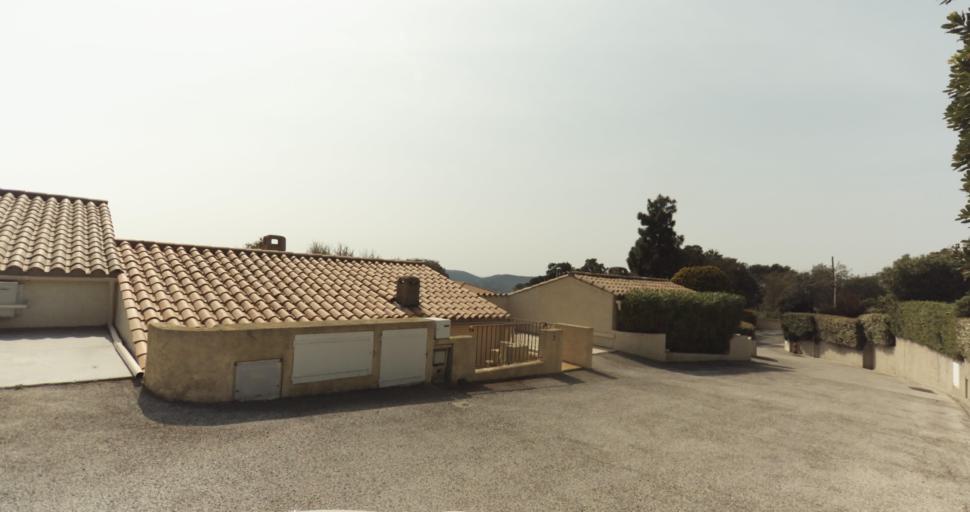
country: FR
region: Provence-Alpes-Cote d'Azur
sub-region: Departement du Var
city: Bormes-les-Mimosas
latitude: 43.1461
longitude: 6.3506
